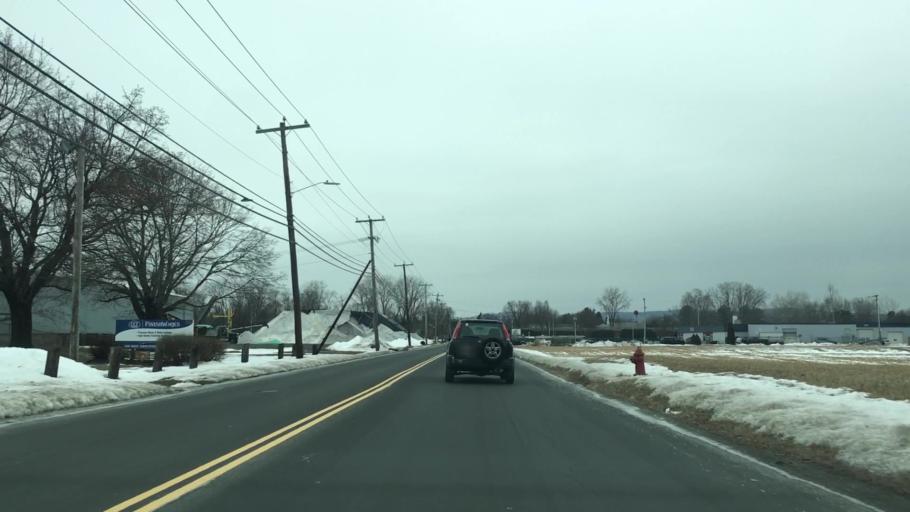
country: US
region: Massachusetts
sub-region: Hampden County
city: Westfield
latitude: 42.1260
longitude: -72.7250
